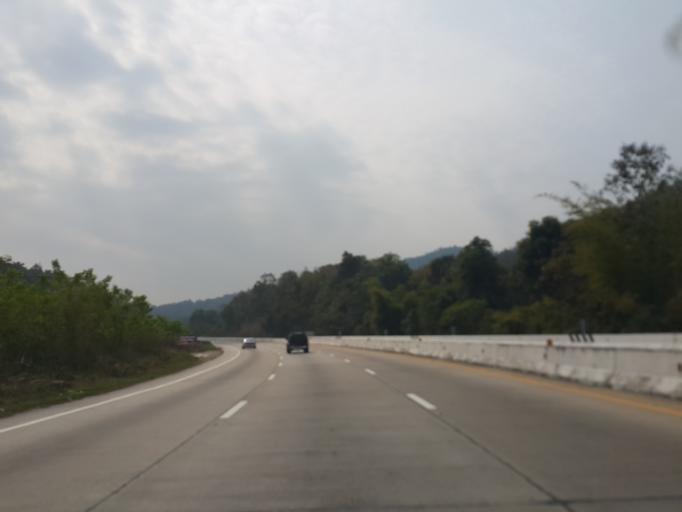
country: TH
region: Lamphun
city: Mae Tha
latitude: 18.4430
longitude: 99.2049
